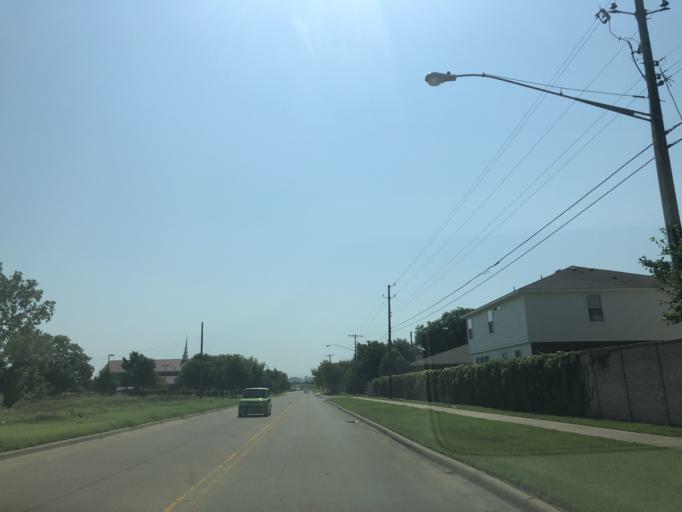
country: US
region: Texas
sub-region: Dallas County
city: Dallas
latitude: 32.7926
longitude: -96.8615
